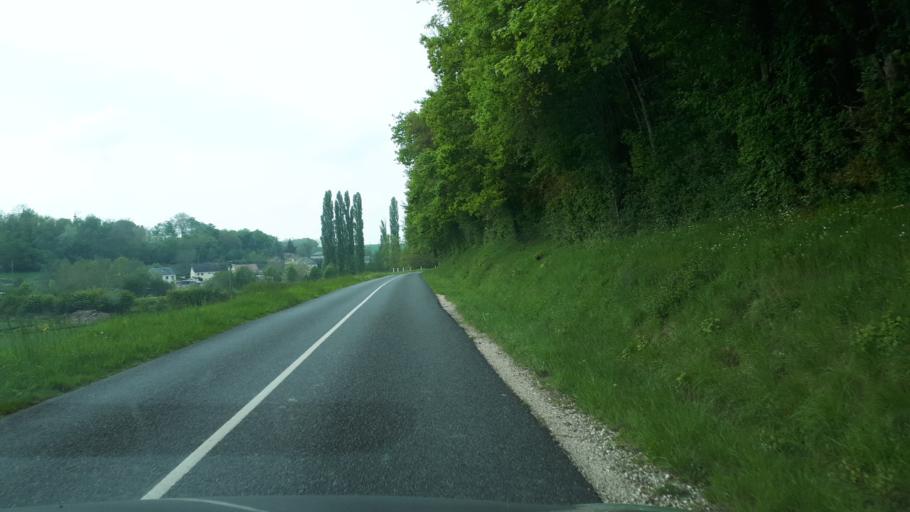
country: FR
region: Centre
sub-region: Departement du Loir-et-Cher
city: Lunay
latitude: 47.8180
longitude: 0.9513
